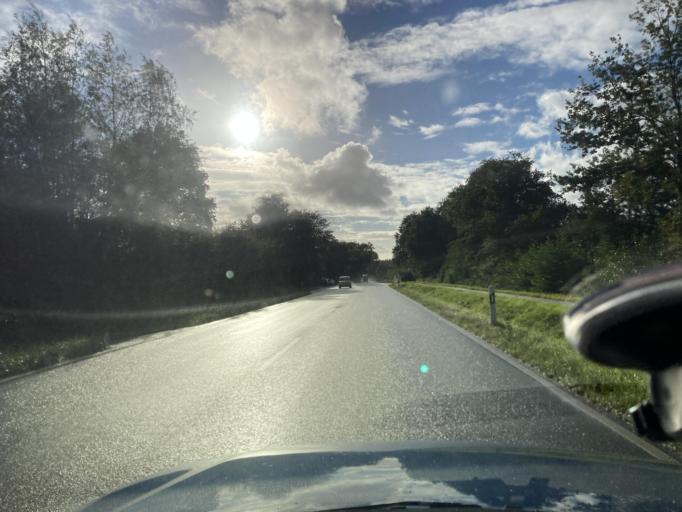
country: DE
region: Schleswig-Holstein
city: Gaushorn
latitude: 54.1956
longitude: 9.2043
